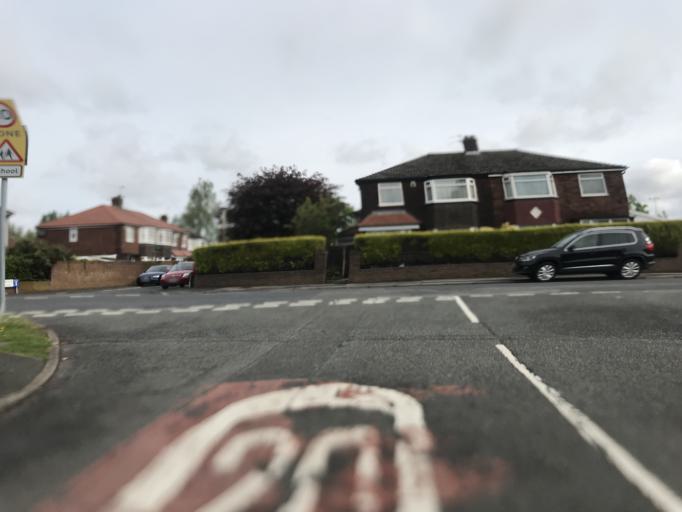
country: GB
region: England
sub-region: Borough of Stockport
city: Cheadle Heath
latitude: 53.4165
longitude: -2.1842
